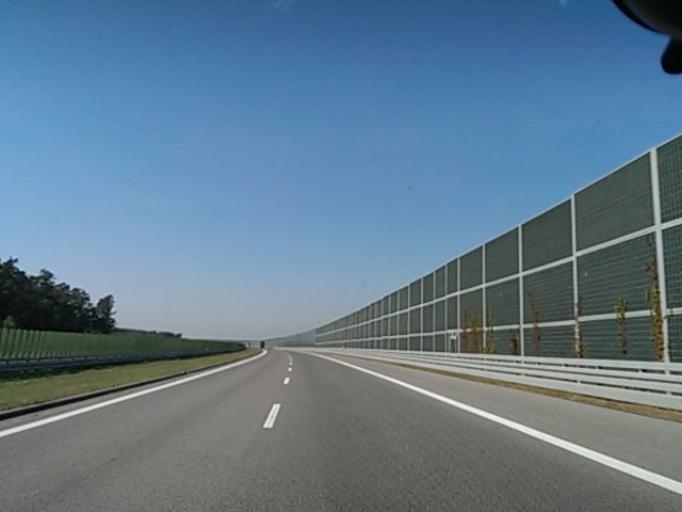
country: PL
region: Subcarpathian Voivodeship
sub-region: Powiat rzeszowski
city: Trzciana
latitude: 50.1183
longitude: 21.7933
